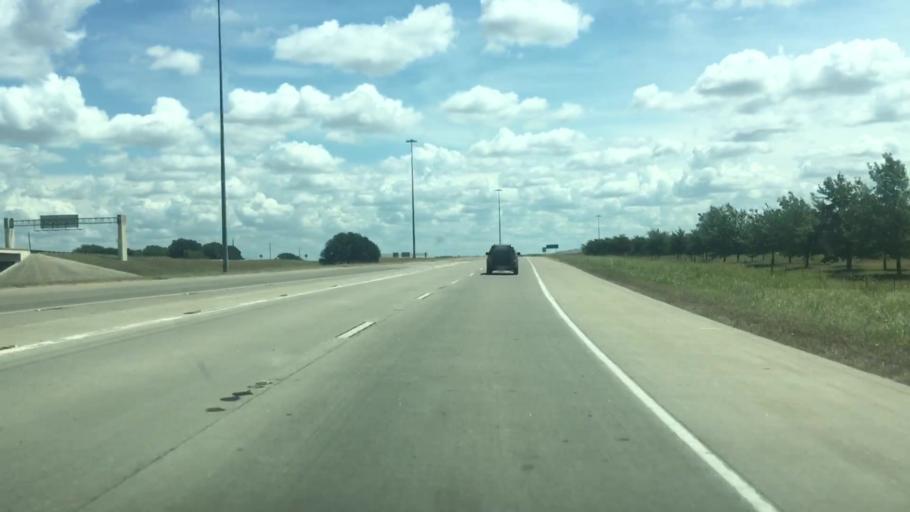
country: US
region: Texas
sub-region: Travis County
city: Onion Creek
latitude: 30.1113
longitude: -97.8038
